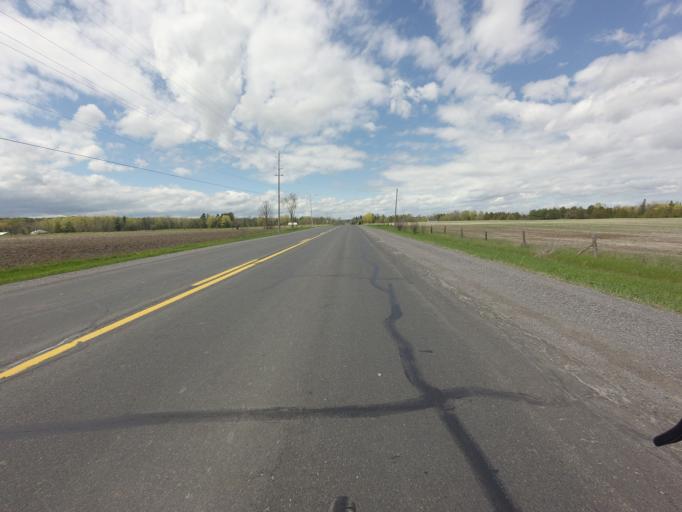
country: CA
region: Ontario
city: Carleton Place
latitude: 45.2504
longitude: -76.2431
